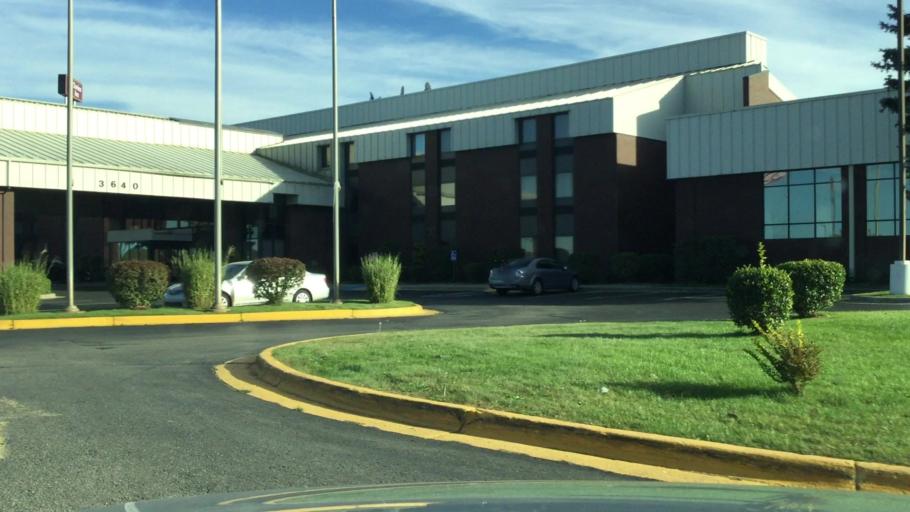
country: US
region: Michigan
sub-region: Kalamazoo County
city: Eastwood
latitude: 42.2612
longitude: -85.5337
